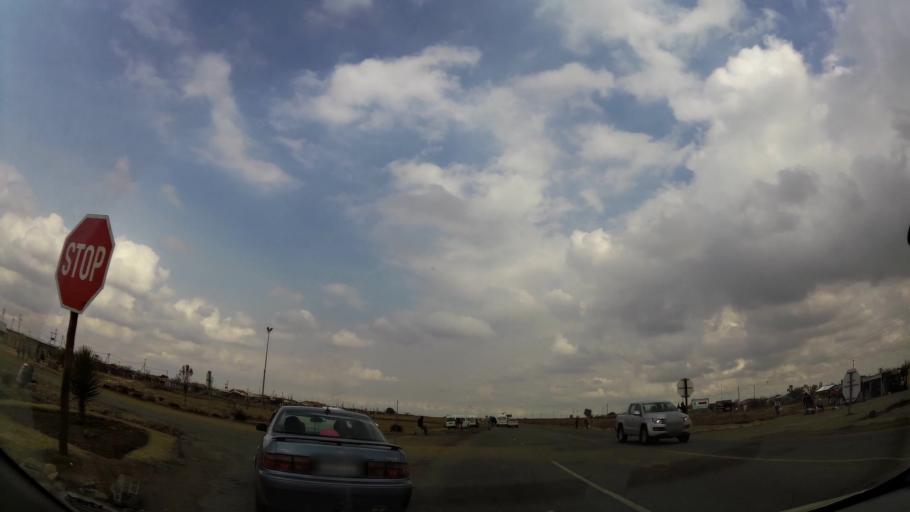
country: ZA
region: Orange Free State
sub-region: Fezile Dabi District Municipality
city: Sasolburg
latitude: -26.8560
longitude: 27.8887
